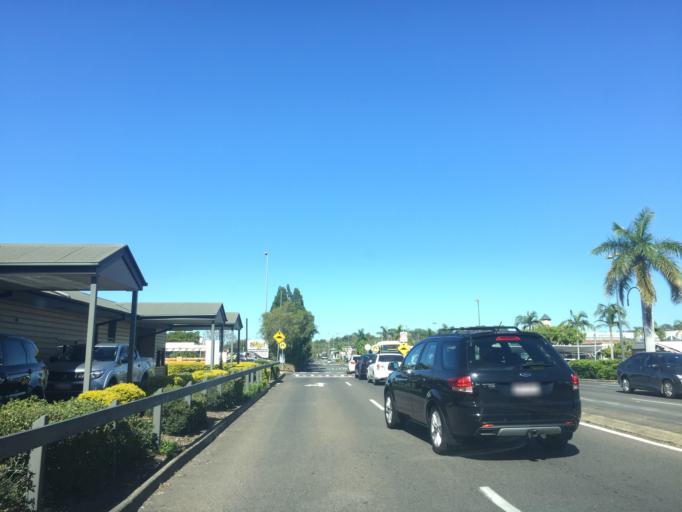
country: AU
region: Queensland
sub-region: Brisbane
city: Stafford
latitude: -27.4103
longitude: 153.0138
